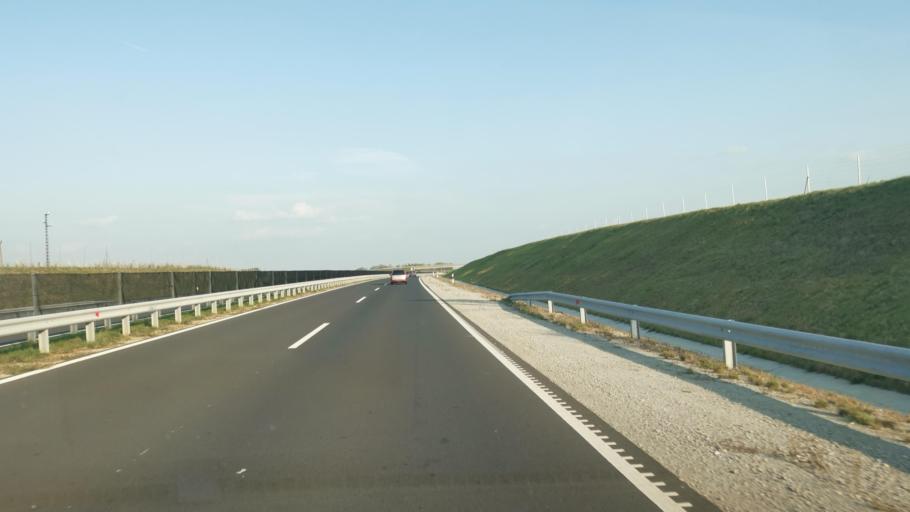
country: HU
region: Gyor-Moson-Sopron
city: Nagycenk
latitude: 47.5816
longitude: 16.7413
